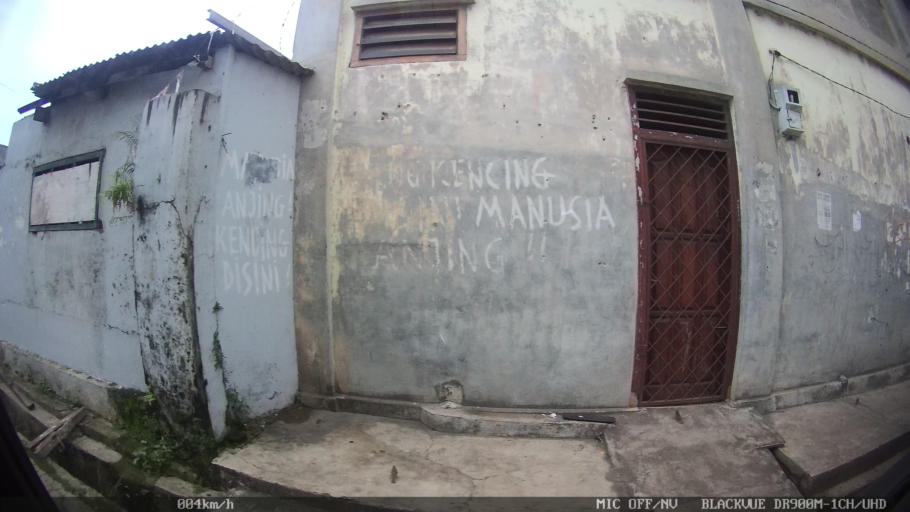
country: ID
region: Lampung
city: Bandarlampung
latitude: -5.4139
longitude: 105.2553
